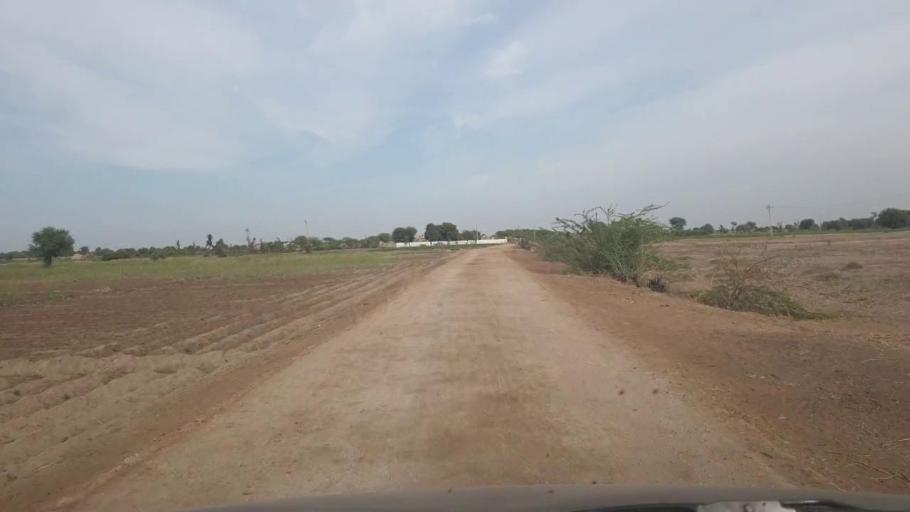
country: PK
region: Sindh
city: Kunri
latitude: 25.2801
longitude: 69.6053
